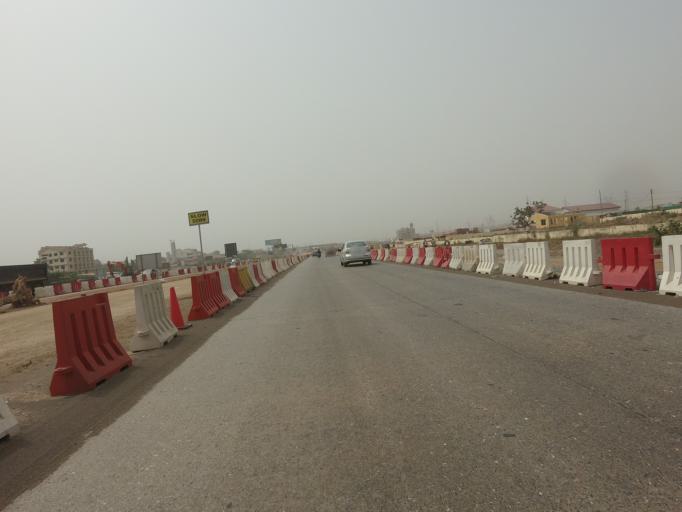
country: GH
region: Greater Accra
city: Tema
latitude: 5.6853
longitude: -0.0189
